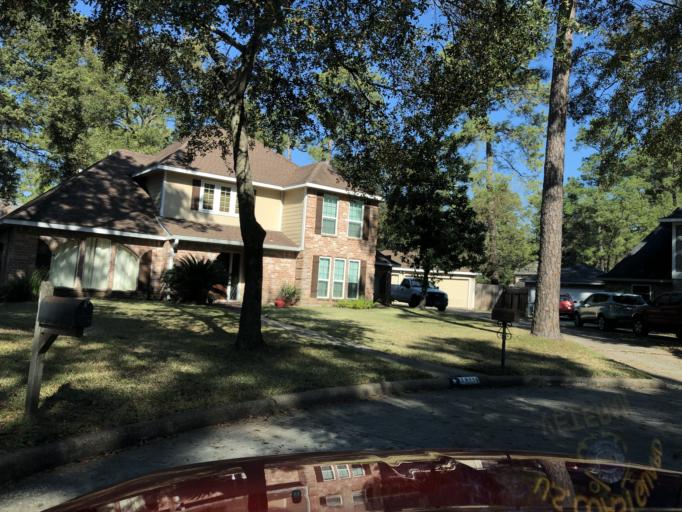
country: US
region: Texas
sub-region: Harris County
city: Tomball
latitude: 30.0271
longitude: -95.5521
